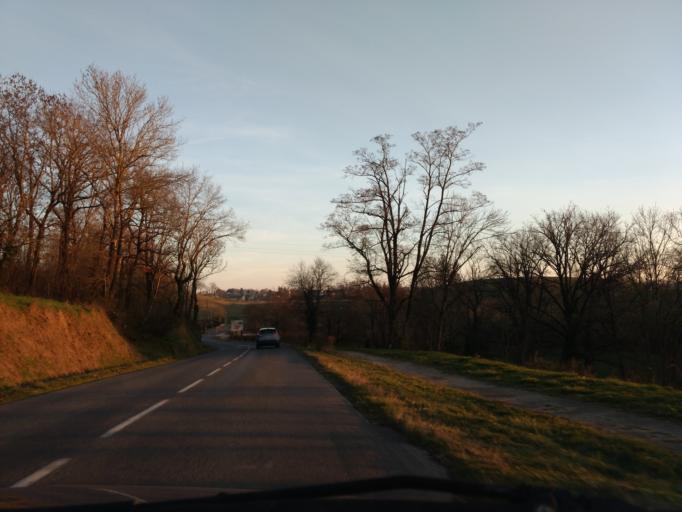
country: FR
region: Midi-Pyrenees
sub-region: Departement de l'Aveyron
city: Naucelle
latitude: 44.1930
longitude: 2.3550
